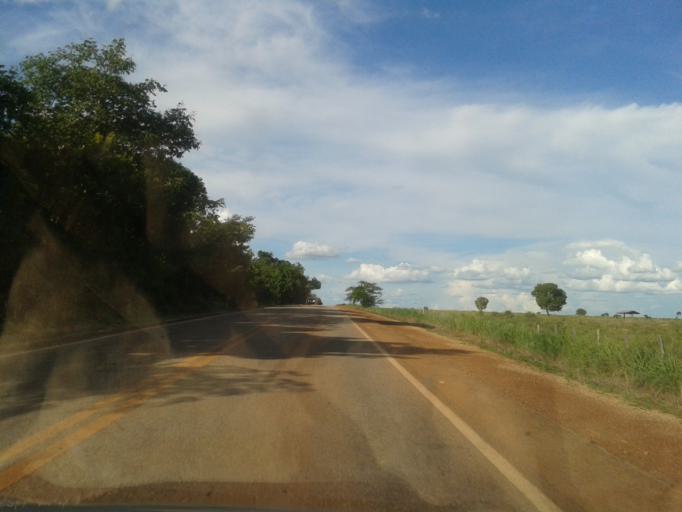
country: BR
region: Goias
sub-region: Mozarlandia
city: Mozarlandia
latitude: -14.3963
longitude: -50.4409
